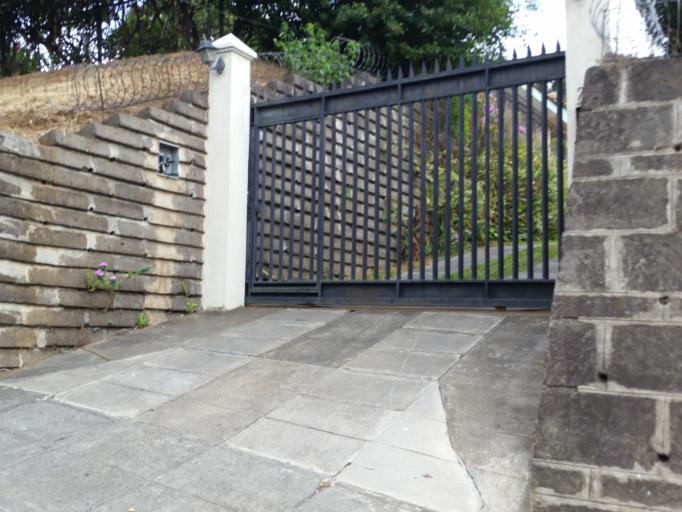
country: NI
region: Managua
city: Managua
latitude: 12.0852
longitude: -86.2473
